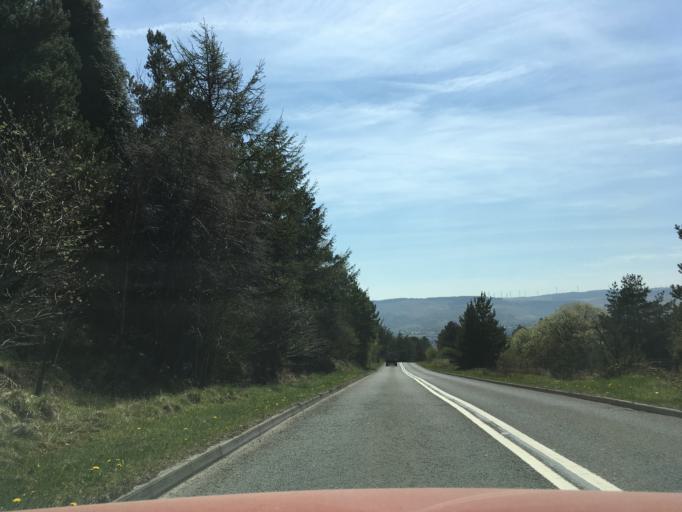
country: GB
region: Wales
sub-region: Rhondda Cynon Taf
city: Aberdare
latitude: 51.7457
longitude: -3.4429
